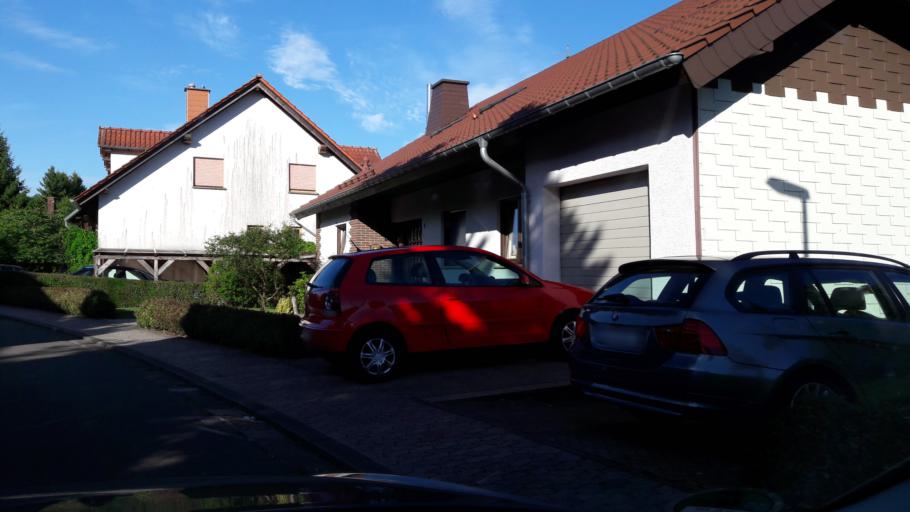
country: DE
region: Saarland
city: Nohfelden
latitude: 49.5574
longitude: 7.1225
